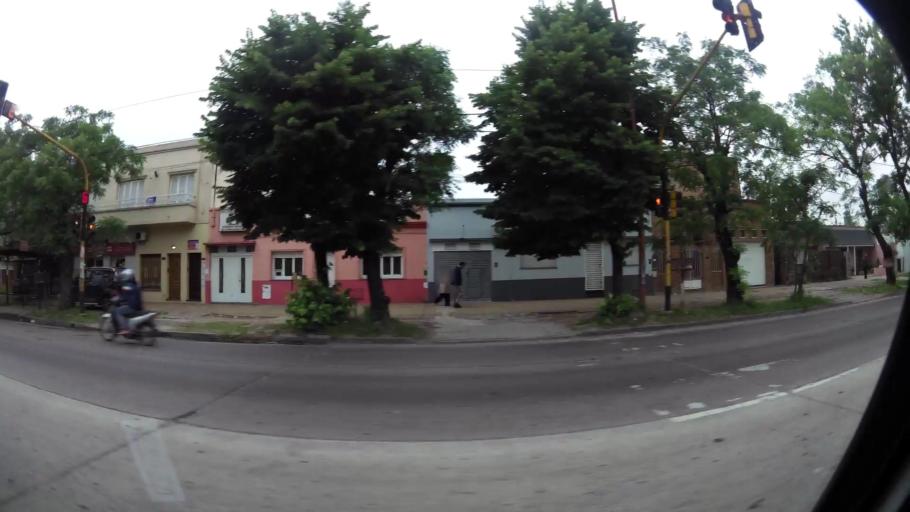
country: AR
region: Buenos Aires
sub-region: Partido de La Plata
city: La Plata
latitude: -34.8888
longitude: -57.9809
